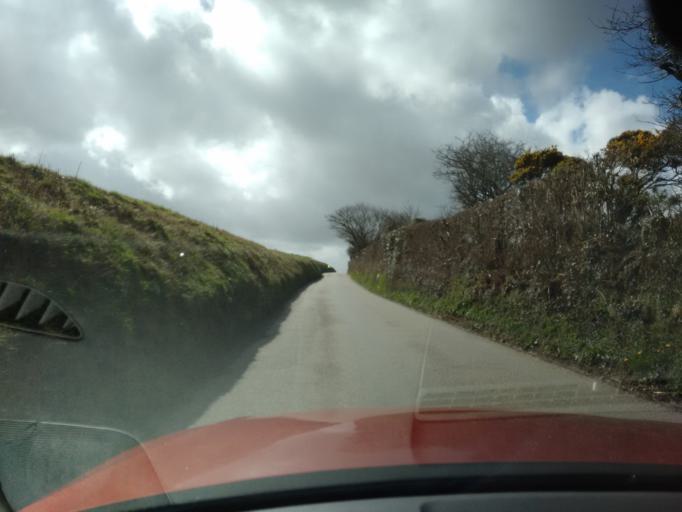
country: GB
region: England
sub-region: Cornwall
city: Liskeard
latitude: 50.4941
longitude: -4.4841
